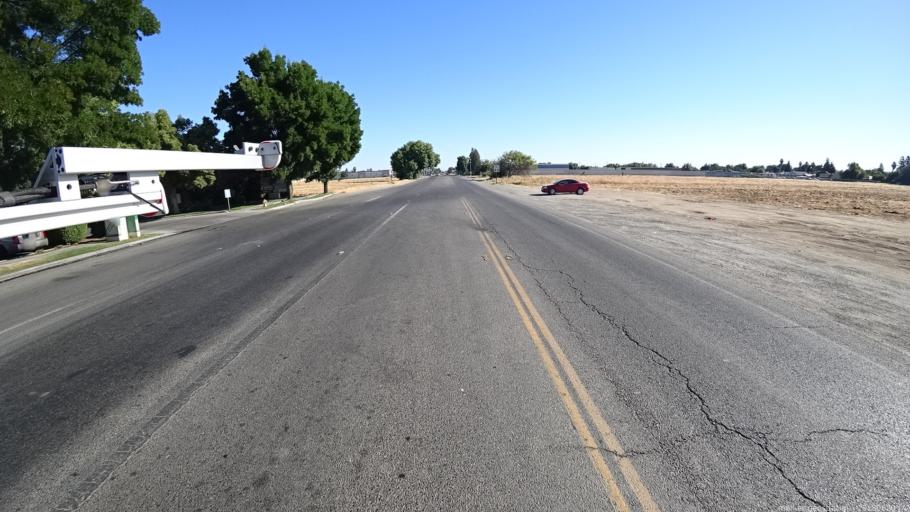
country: US
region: California
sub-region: Madera County
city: Parkwood
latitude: 36.9387
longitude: -120.0560
